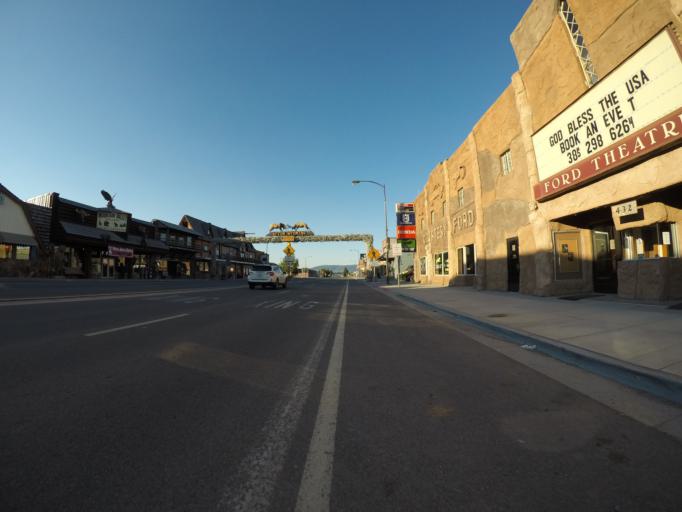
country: US
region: Wyoming
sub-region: Lincoln County
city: Afton
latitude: 42.7246
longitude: -110.9336
